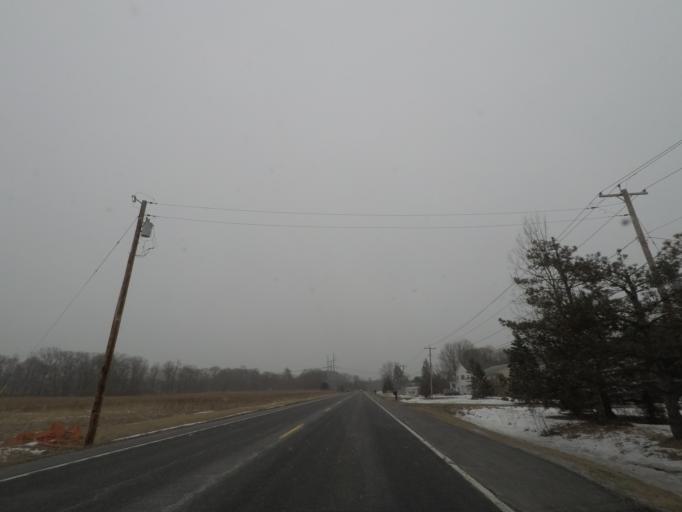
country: US
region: New York
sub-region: Albany County
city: Delmar
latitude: 42.5608
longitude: -73.8176
